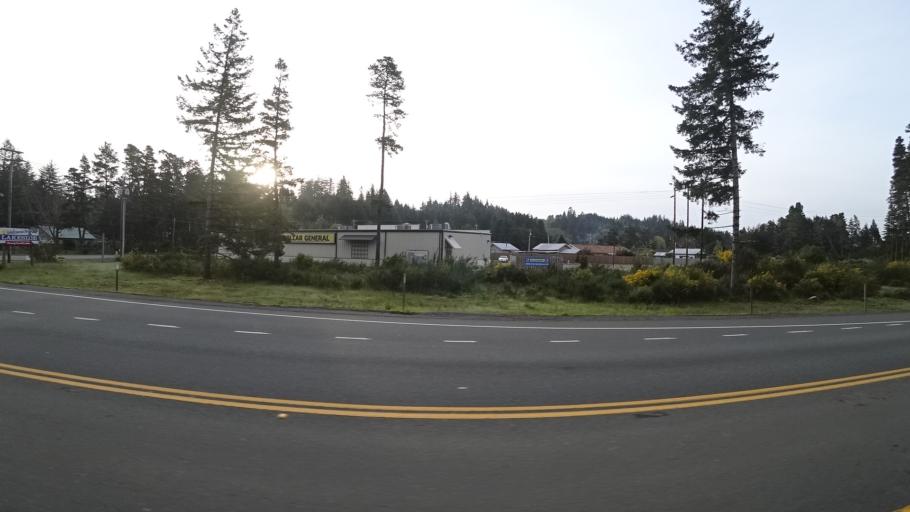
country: US
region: Oregon
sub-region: Coos County
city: Lakeside
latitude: 43.5909
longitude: -124.1830
